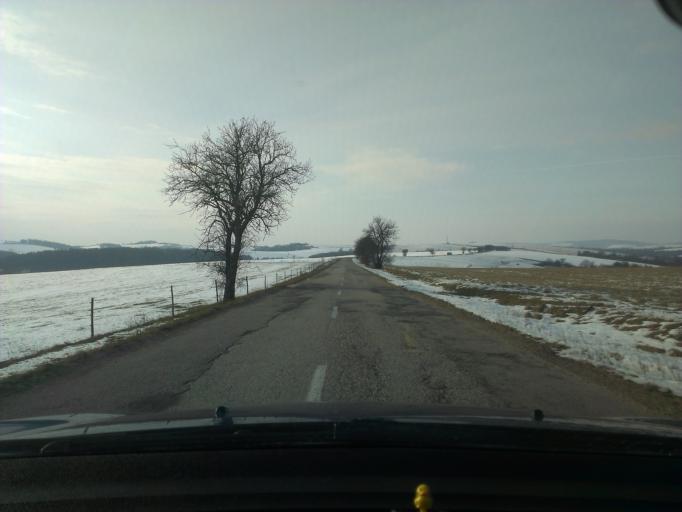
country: SK
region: Nitriansky
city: Stara Tura
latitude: 48.7498
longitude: 17.6363
